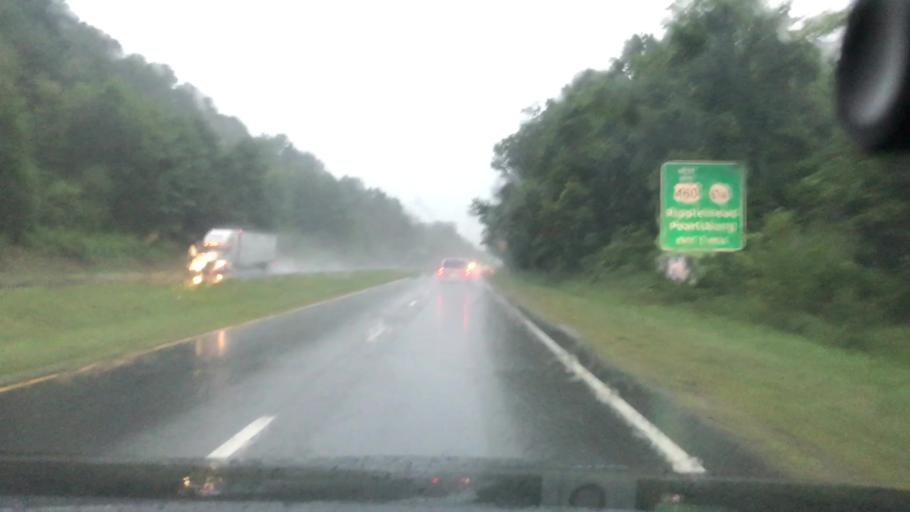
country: US
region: Virginia
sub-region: Giles County
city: Pearisburg
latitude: 37.3386
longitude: -80.7148
